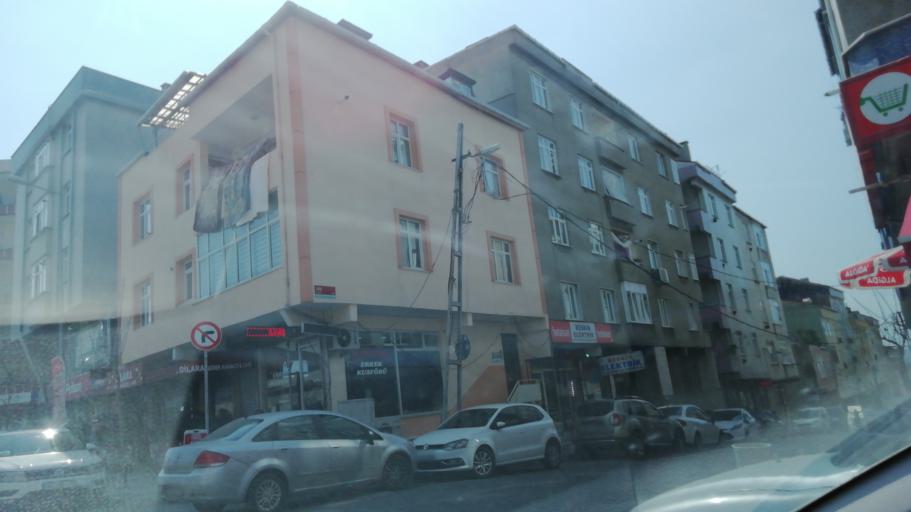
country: TR
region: Istanbul
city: Mahmutbey
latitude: 41.0362
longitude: 28.8198
